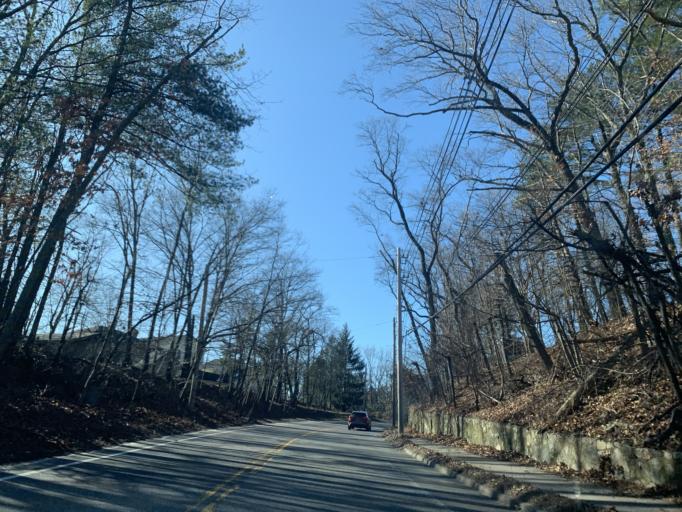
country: US
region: Massachusetts
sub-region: Middlesex County
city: Sudbury
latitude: 42.3616
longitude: -71.4068
